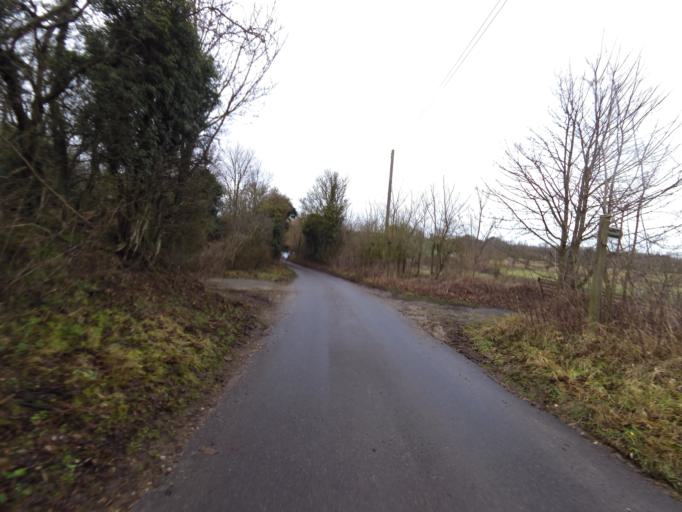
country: GB
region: England
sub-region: Suffolk
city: Needham Market
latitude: 52.1625
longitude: 1.0623
